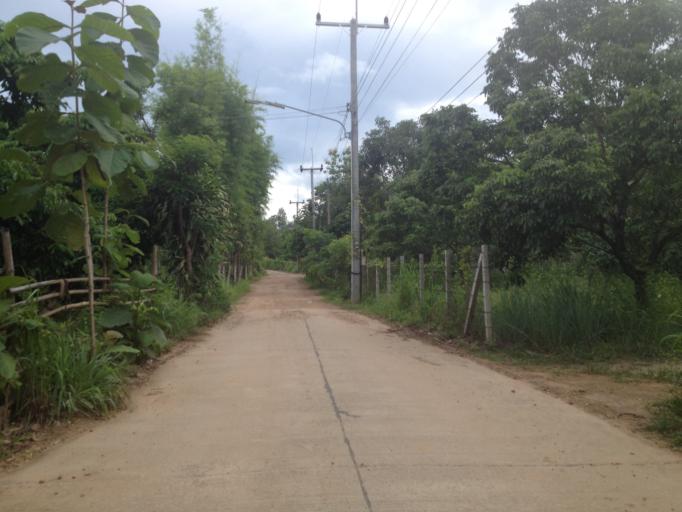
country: TH
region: Chiang Mai
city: Hang Dong
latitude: 18.6951
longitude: 98.8847
